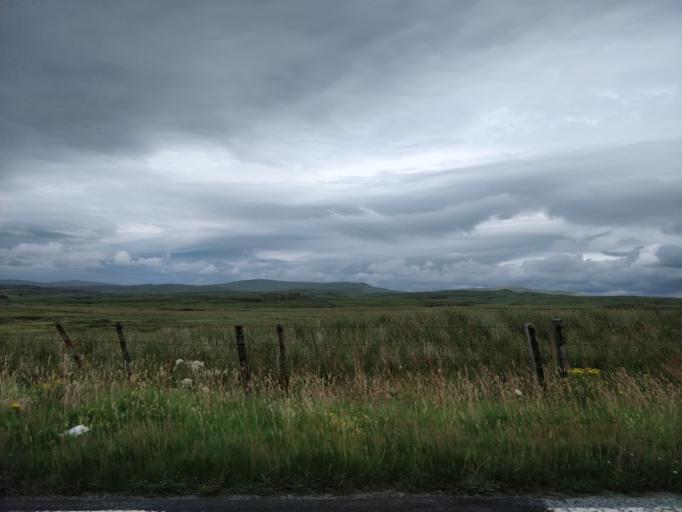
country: GB
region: Scotland
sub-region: Highland
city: Isle of Skye
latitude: 57.3705
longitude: -6.4550
